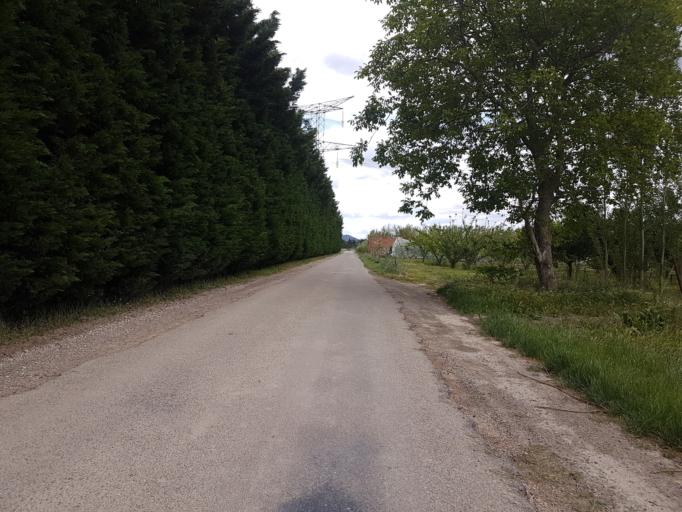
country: FR
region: Languedoc-Roussillon
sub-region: Departement du Gard
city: Vallabregues
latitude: 43.8771
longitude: 4.6270
